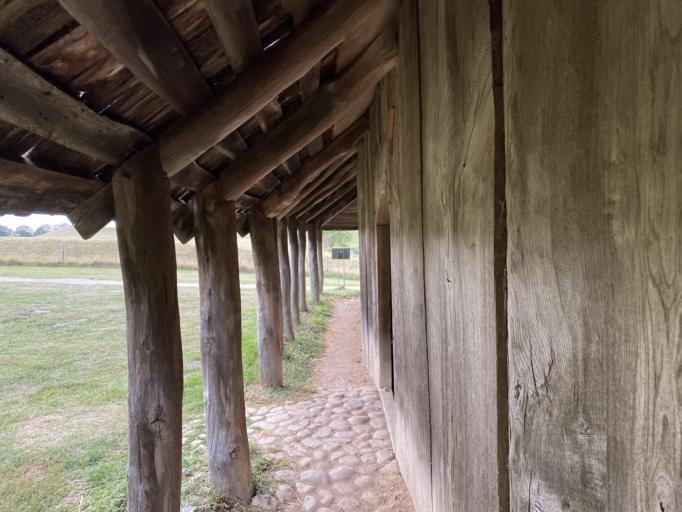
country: DK
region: Zealand
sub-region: Slagelse Kommune
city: Forlev
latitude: 55.3939
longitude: 11.2697
